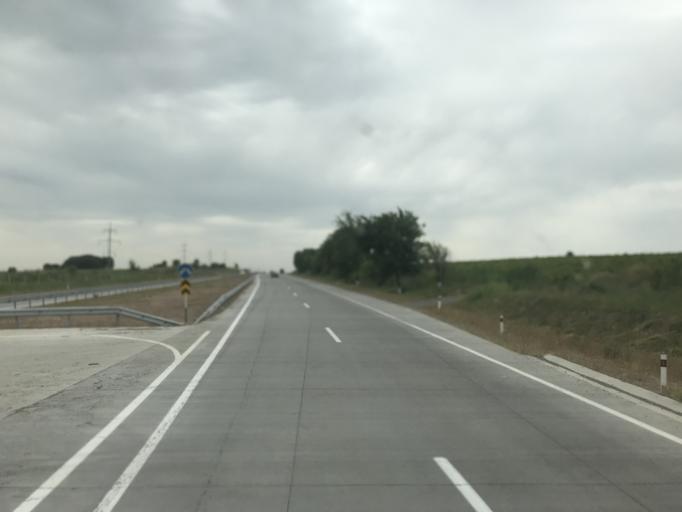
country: KZ
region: Ongtustik Qazaqstan
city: Qazyqurt
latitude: 41.5959
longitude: 69.4057
